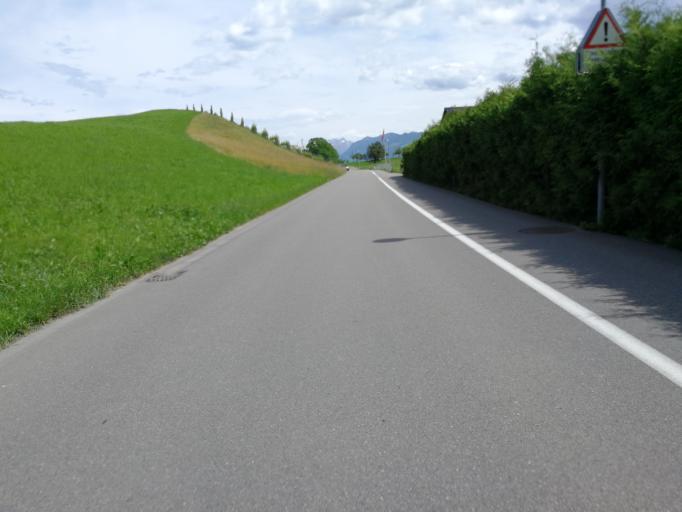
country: CH
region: Zurich
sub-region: Bezirk Hinwil
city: Wolfhausen
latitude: 47.2461
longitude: 8.8141
